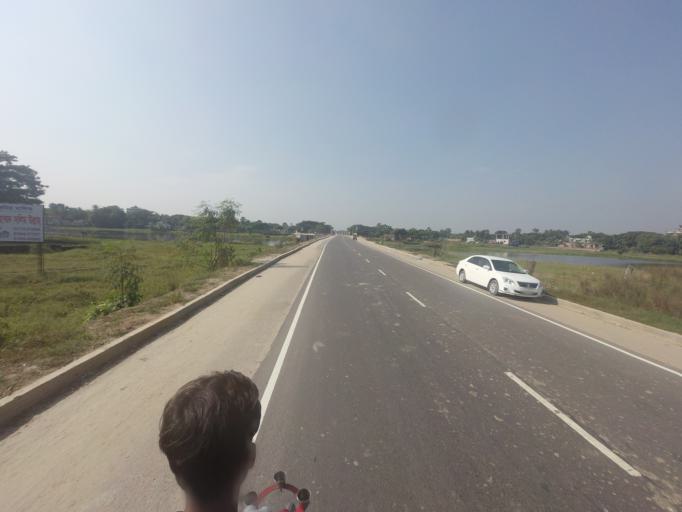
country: BD
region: Dhaka
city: Azimpur
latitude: 23.7337
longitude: 90.3331
